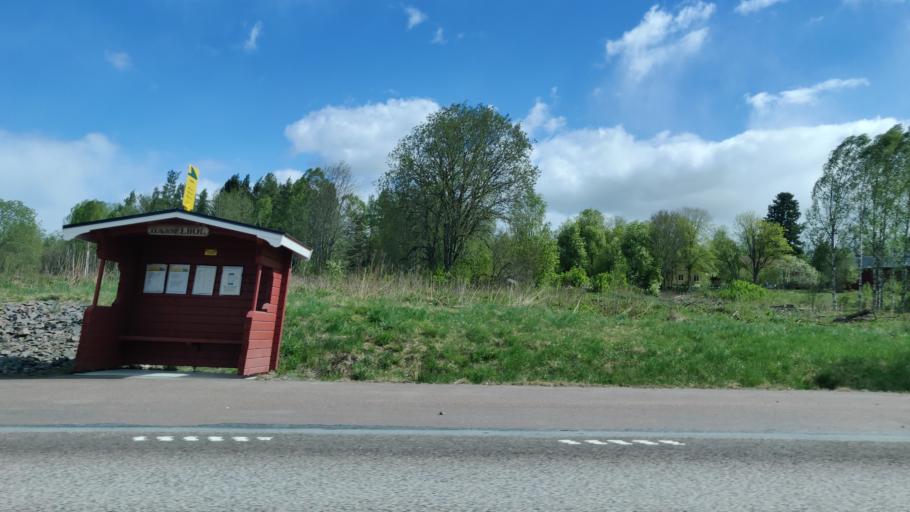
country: SE
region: Vaermland
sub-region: Karlstads Kommun
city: Molkom
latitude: 59.5331
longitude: 13.6185
